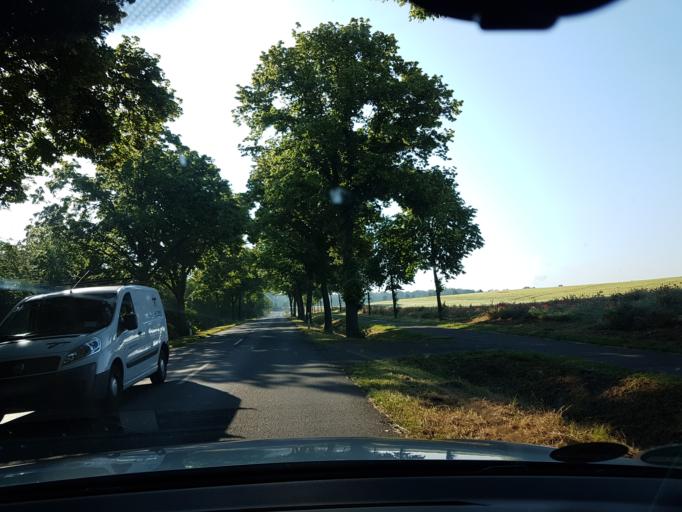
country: DE
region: Lower Saxony
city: Helmstedt
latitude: 52.2179
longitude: 11.0359
